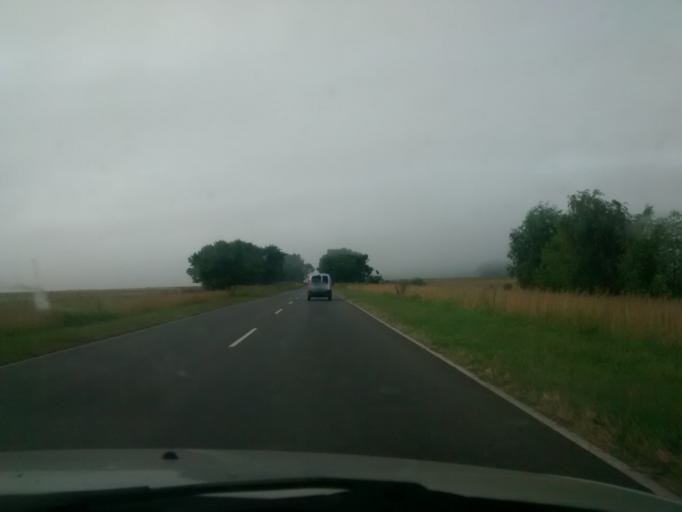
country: AR
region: Buenos Aires
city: Ranchos
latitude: -35.3514
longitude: -58.2478
